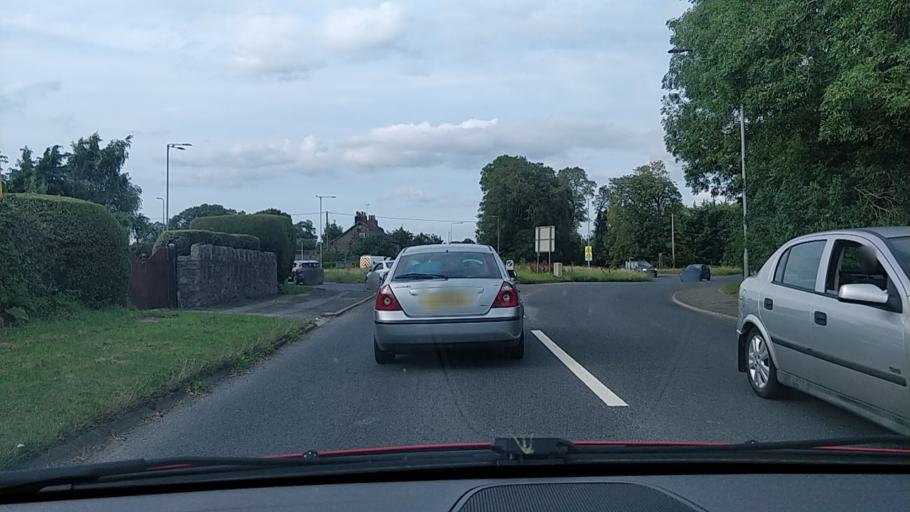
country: GB
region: Wales
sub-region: County of Flintshire
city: Penyffordd
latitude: 53.1569
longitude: -3.0428
